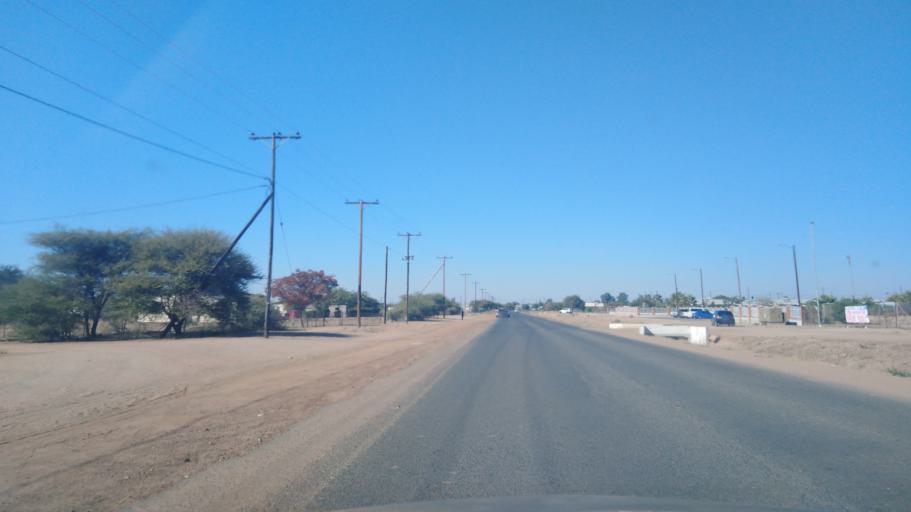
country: BW
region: Central
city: Mahalapye
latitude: -23.1202
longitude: 26.7942
